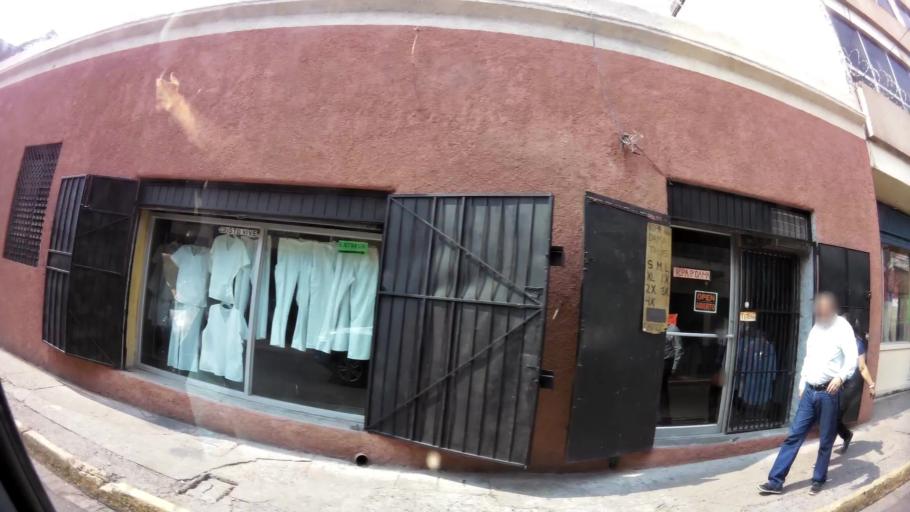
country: HN
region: Francisco Morazan
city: Tegucigalpa
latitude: 14.1069
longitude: -87.2023
